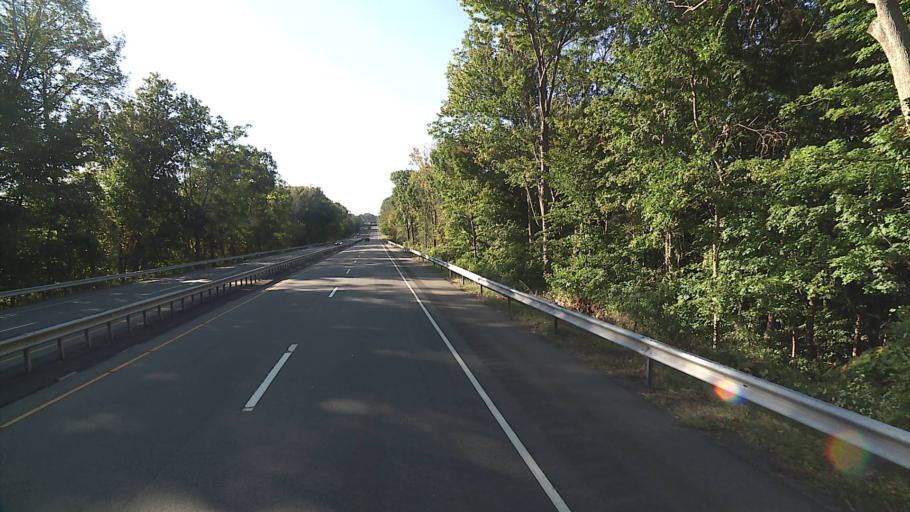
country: US
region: Connecticut
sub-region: New Haven County
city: Meriden
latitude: 41.5476
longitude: -72.7729
